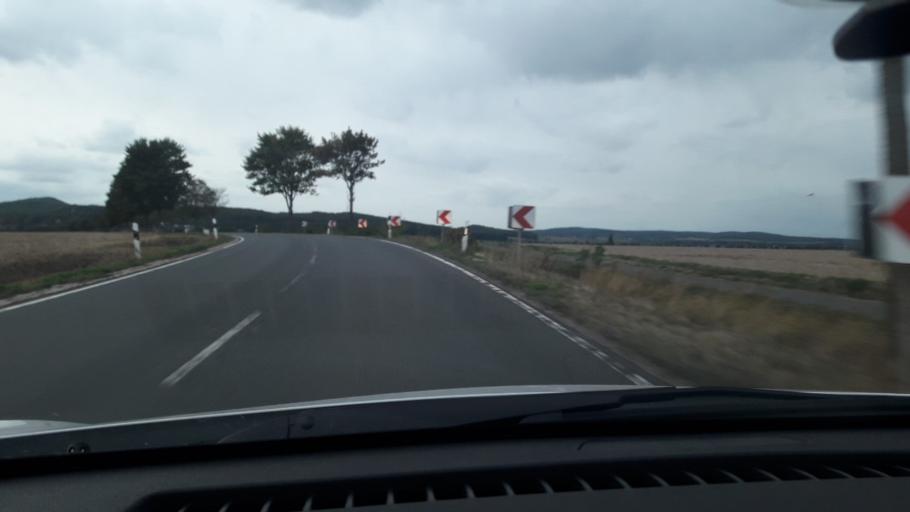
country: DE
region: Lower Saxony
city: Liebenburg
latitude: 52.0217
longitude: 10.4594
